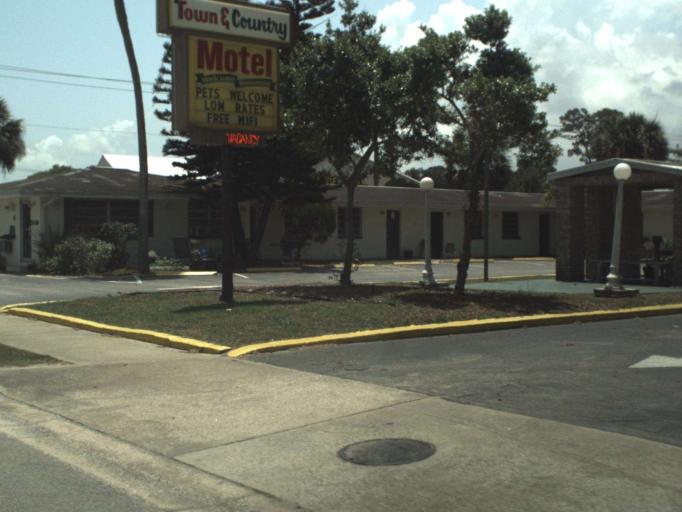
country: US
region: Florida
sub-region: Volusia County
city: Port Orange
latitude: 29.1220
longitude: -80.9769
